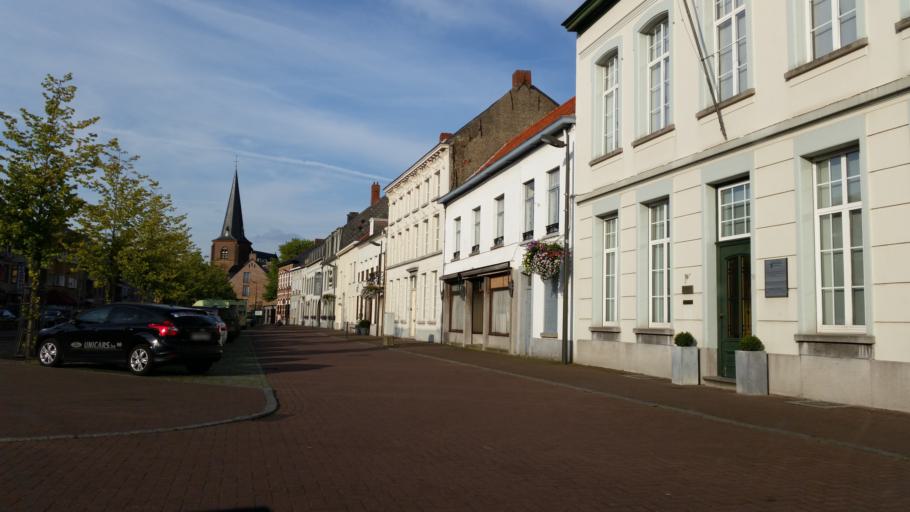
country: BE
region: Flanders
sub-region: Provincie Antwerpen
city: Westerlo
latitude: 51.0870
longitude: 4.9178
